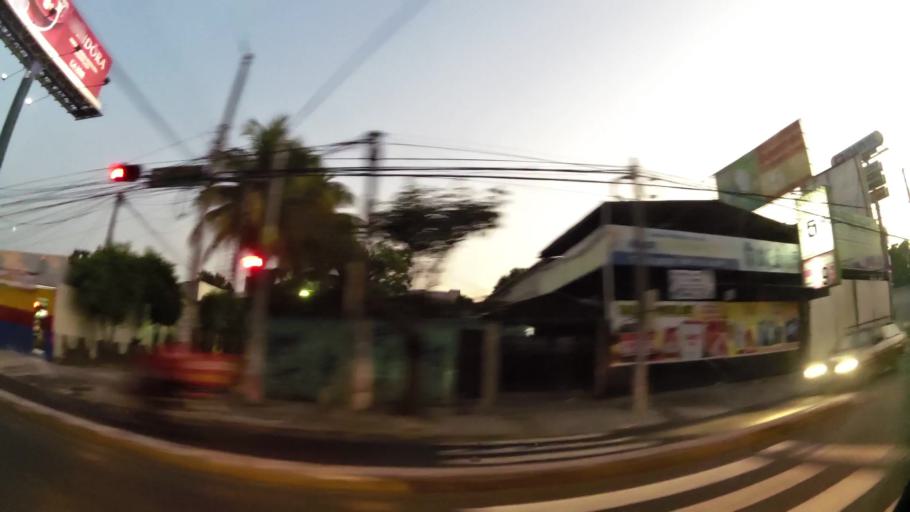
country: SV
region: La Libertad
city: Antiguo Cuscatlan
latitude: 13.6784
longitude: -89.2564
